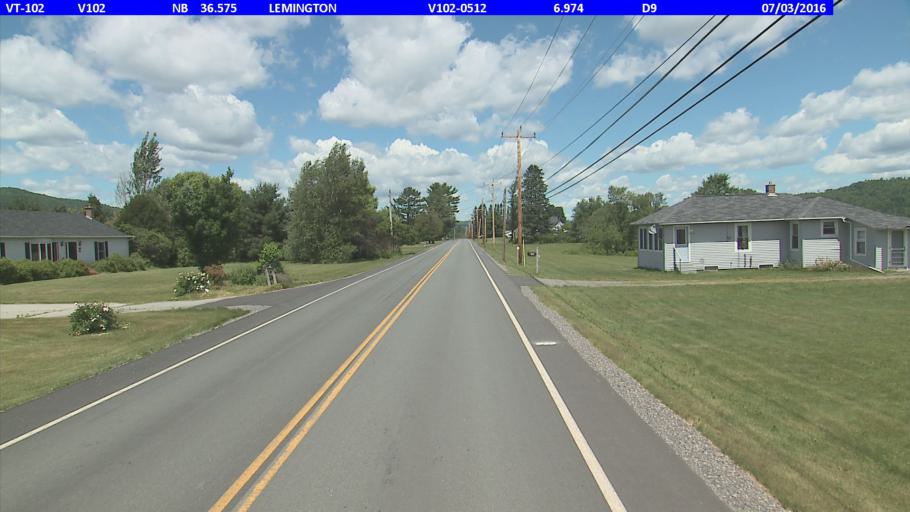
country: US
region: New Hampshire
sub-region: Coos County
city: Colebrook
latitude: 44.9064
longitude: -71.5034
